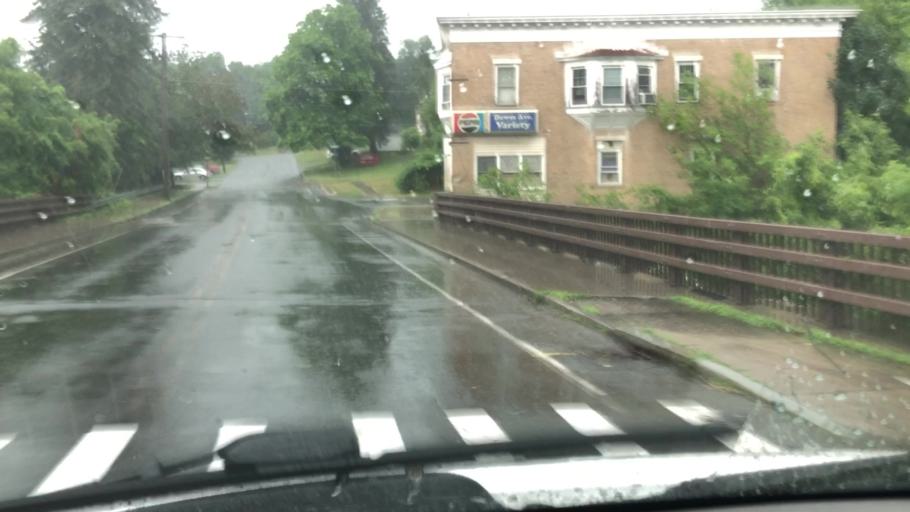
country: US
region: Massachusetts
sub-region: Berkshire County
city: Pittsfield
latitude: 42.4405
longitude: -73.2481
